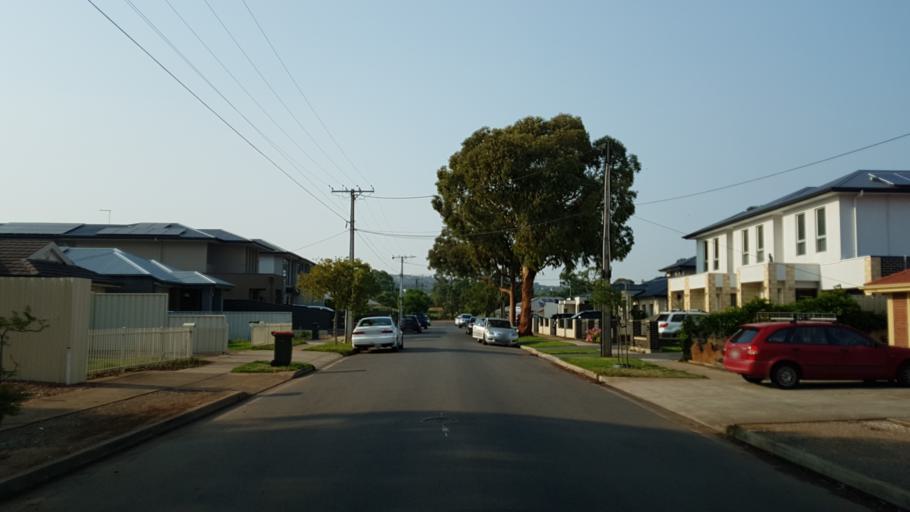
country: AU
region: South Australia
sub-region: Holdfast Bay
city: Seacliff Park
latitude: -35.0209
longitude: 138.5370
